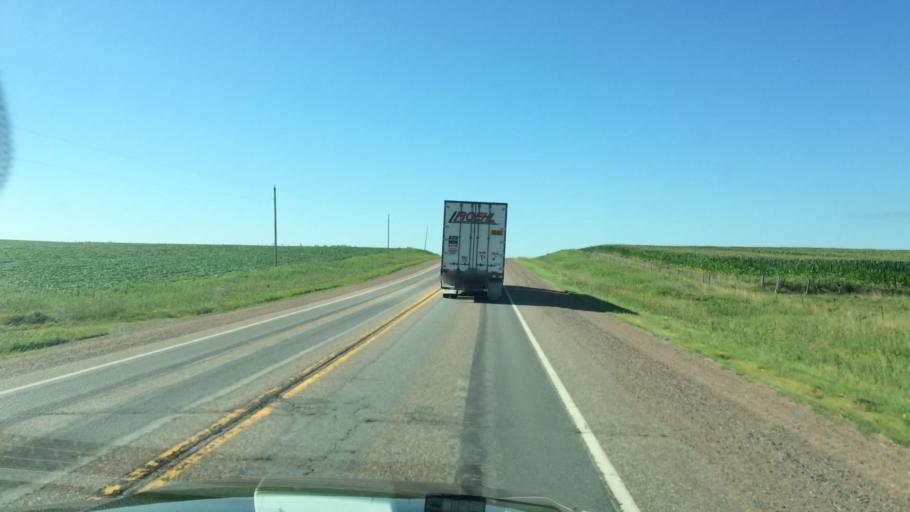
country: US
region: Wisconsin
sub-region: Marathon County
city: Athens
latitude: 44.9226
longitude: -90.0787
